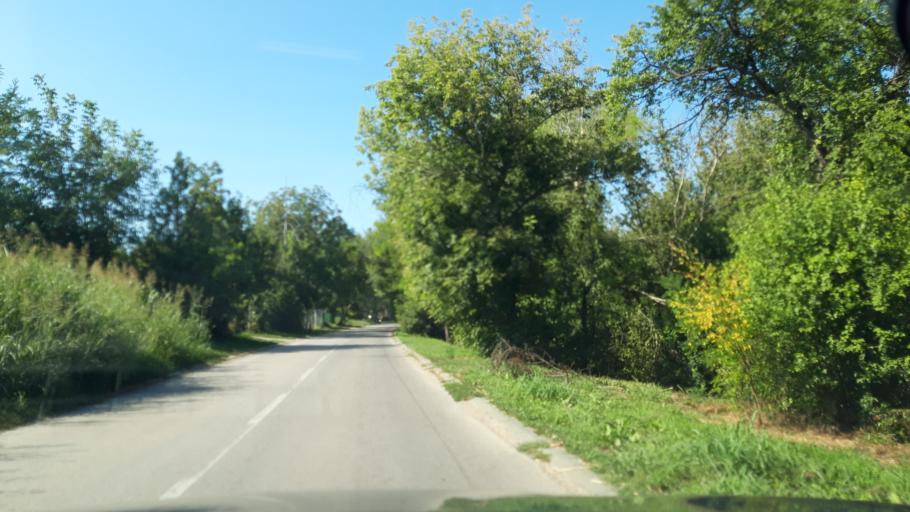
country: RS
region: Autonomna Pokrajina Vojvodina
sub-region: Sremski Okrug
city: Ruma
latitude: 45.0313
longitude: 19.8202
